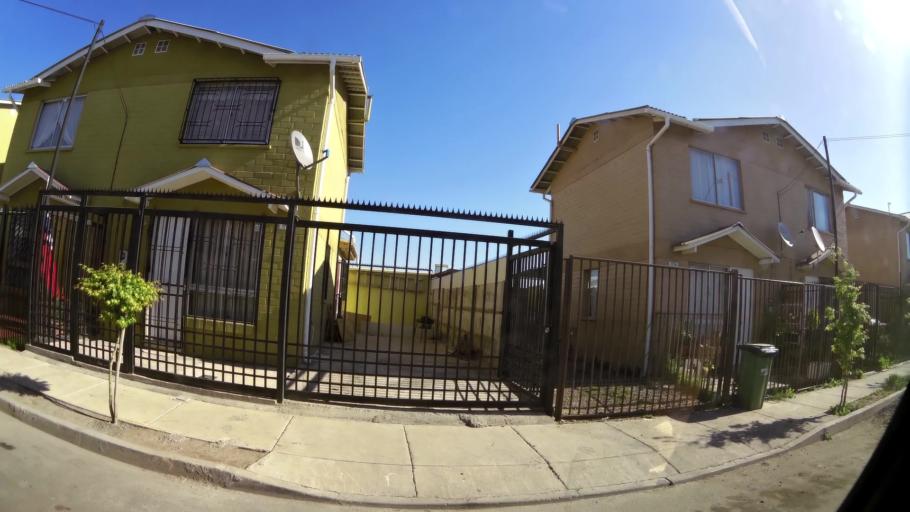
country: CL
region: Santiago Metropolitan
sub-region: Provincia de Talagante
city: Penaflor
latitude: -33.6175
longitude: -70.8790
